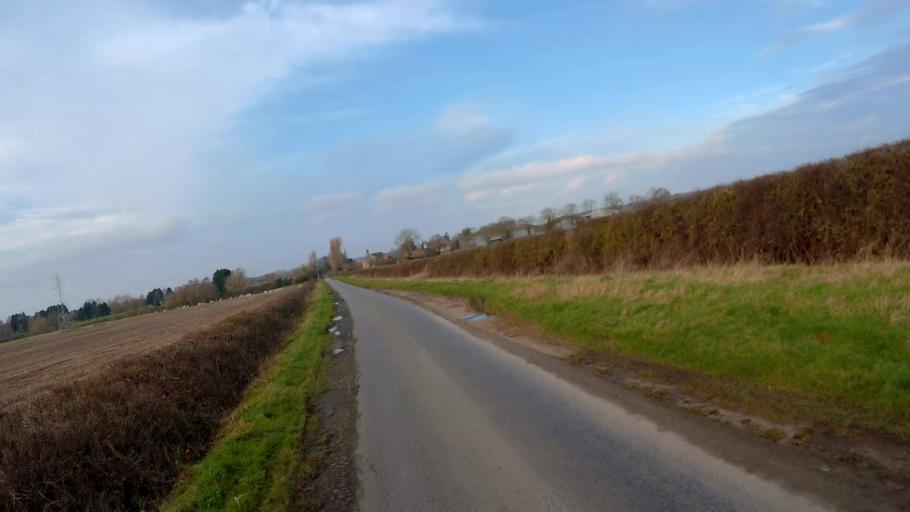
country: GB
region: England
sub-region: Lincolnshire
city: Bourne
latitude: 52.7398
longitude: -0.4033
